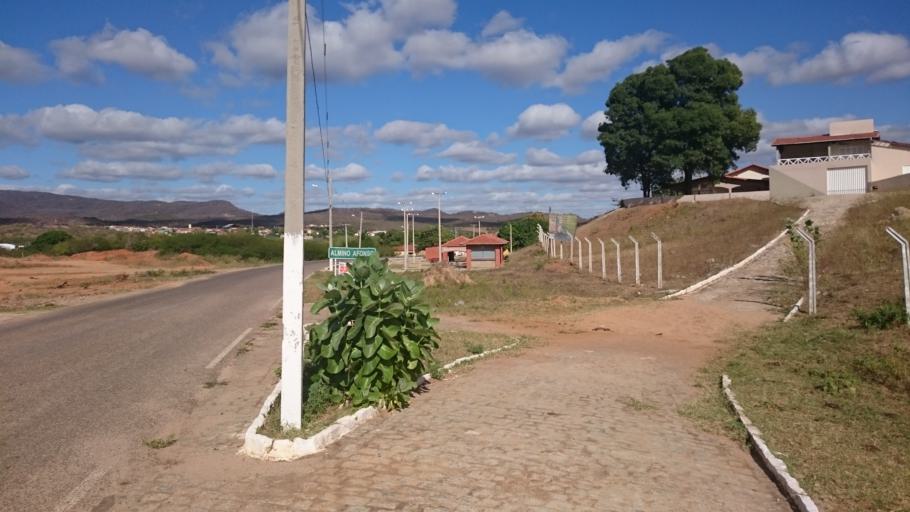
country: BR
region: Paraiba
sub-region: Catole Do Rocha
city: Sao Bento
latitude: -6.1537
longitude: -37.7616
